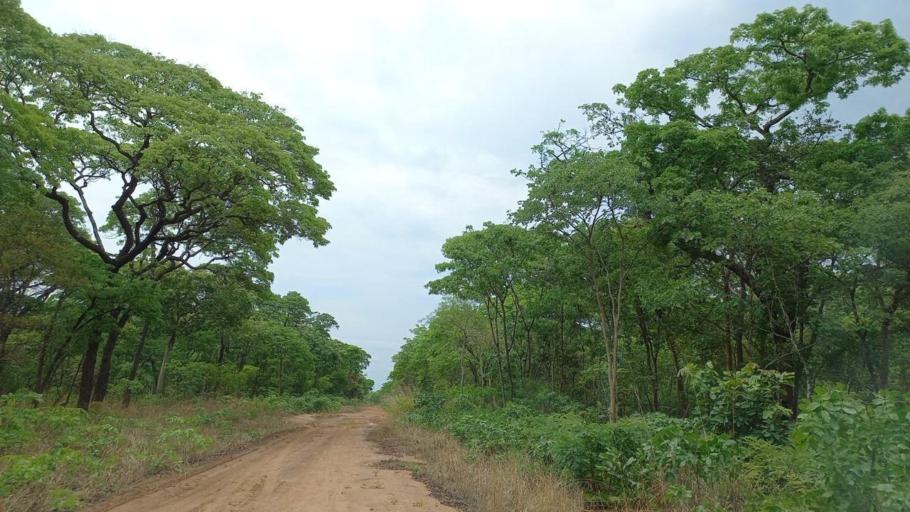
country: ZM
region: North-Western
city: Kalengwa
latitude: -13.5733
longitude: 24.9706
